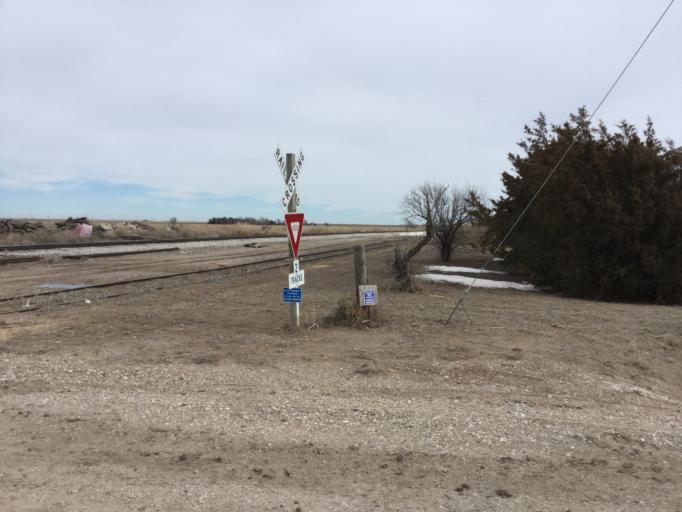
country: US
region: Kansas
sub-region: Lane County
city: Dighton
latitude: 38.4830
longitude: -100.6015
